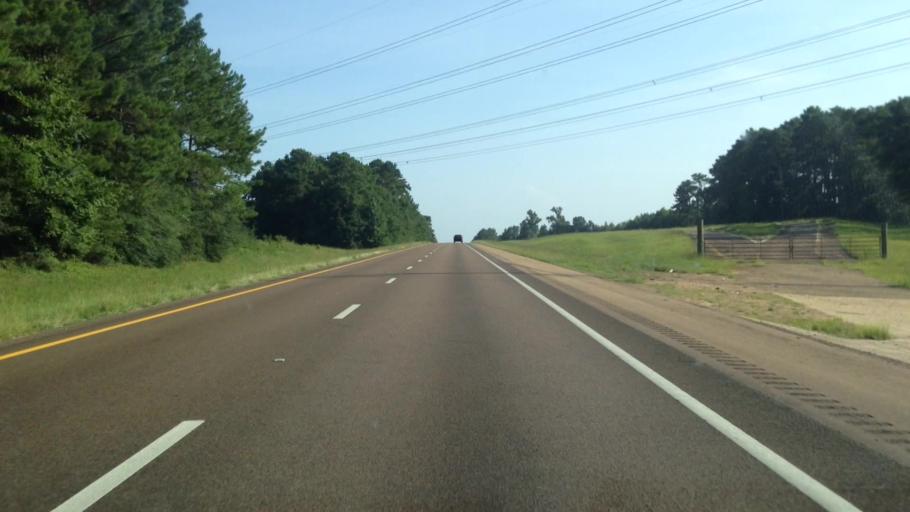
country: US
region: Mississippi
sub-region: Pike County
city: Summit
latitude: 31.3656
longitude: -90.4791
